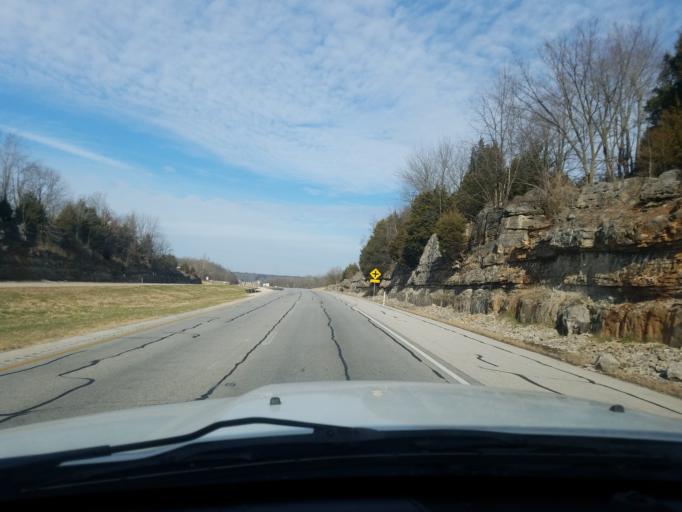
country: US
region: Indiana
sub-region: Lawrence County
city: Oolitic
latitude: 38.9886
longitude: -86.5374
